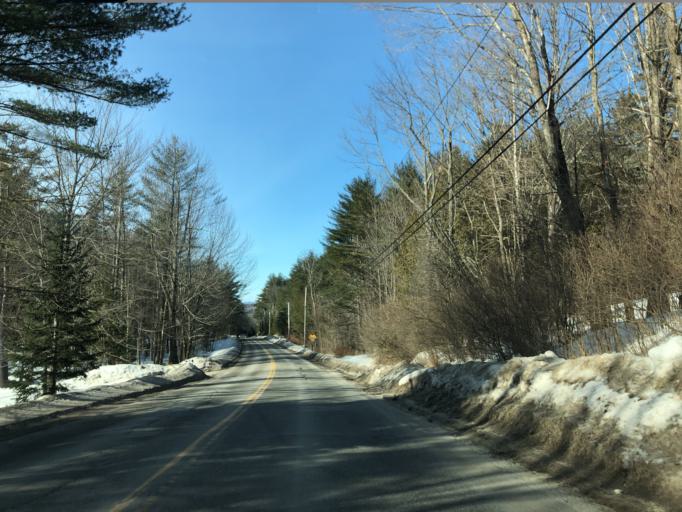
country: US
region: Maine
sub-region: Androscoggin County
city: Mechanic Falls
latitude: 44.1615
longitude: -70.3583
